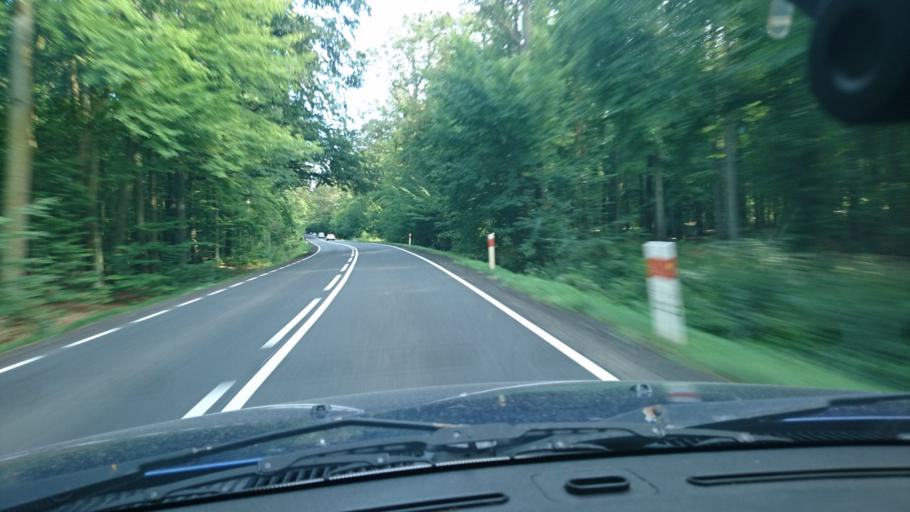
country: PL
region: Greater Poland Voivodeship
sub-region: Powiat krotoszynski
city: Krotoszyn
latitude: 51.6630
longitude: 17.4679
